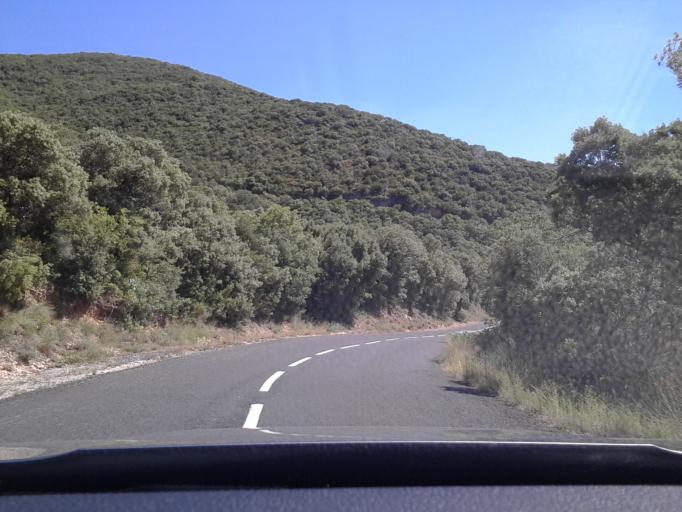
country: FR
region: Languedoc-Roussillon
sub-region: Departement de l'Herault
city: Montpeyroux
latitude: 43.7306
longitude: 3.4628
